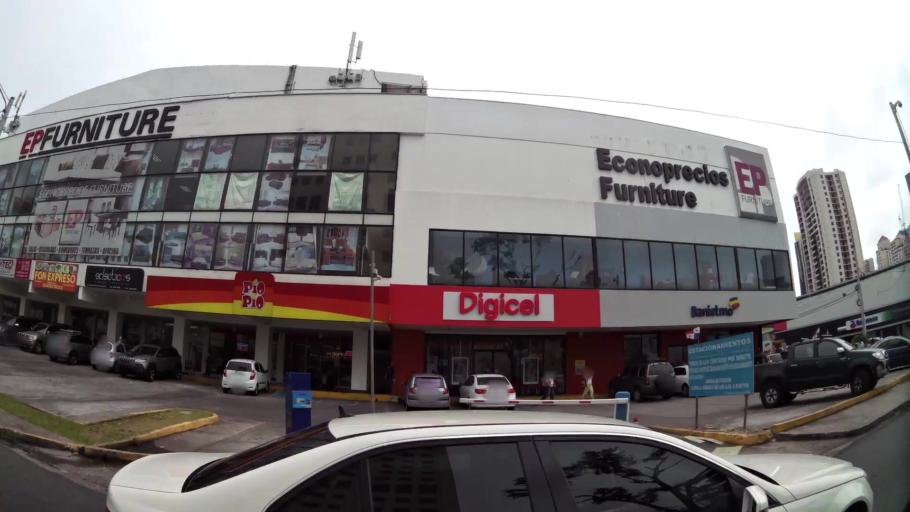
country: PA
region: Panama
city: Panama
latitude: 8.9903
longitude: -79.5217
